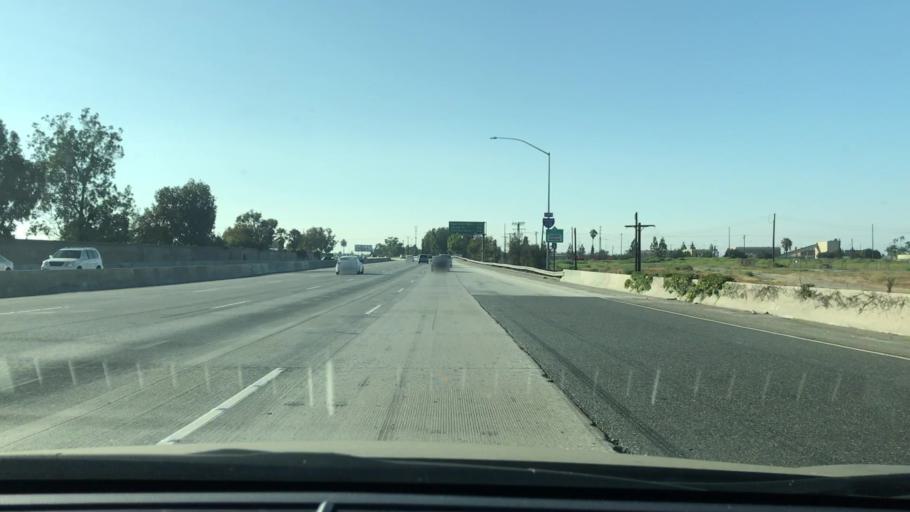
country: US
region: California
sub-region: Los Angeles County
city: West Carson
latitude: 33.7943
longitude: -118.2840
